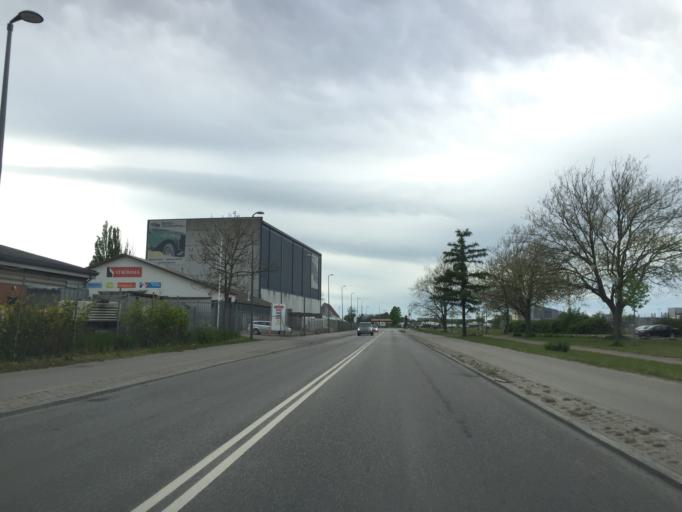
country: DK
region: Capital Region
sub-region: Kobenhavn
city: Christianshavn
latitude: 55.6682
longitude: 12.6266
